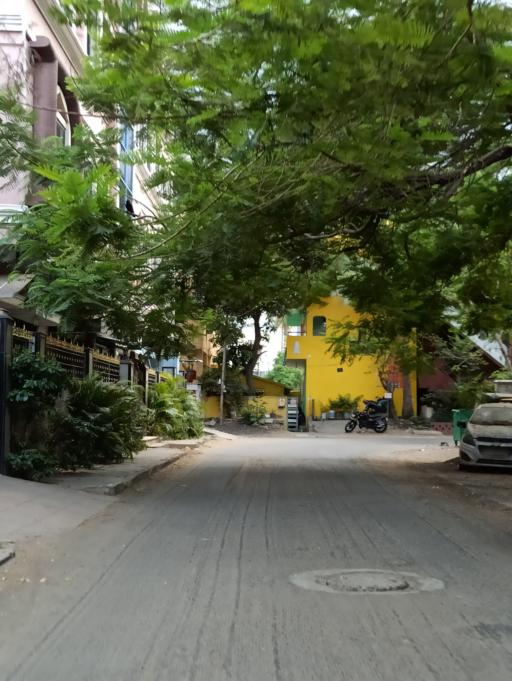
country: IN
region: Tamil Nadu
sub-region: Chennai
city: Chetput
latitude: 13.0559
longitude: 80.2076
